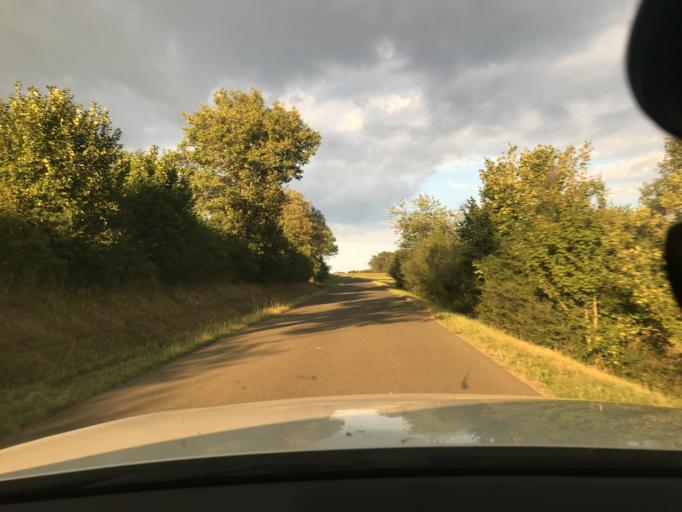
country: DE
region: Bavaria
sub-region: Upper Franconia
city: Pegnitz
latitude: 49.7454
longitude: 11.5683
